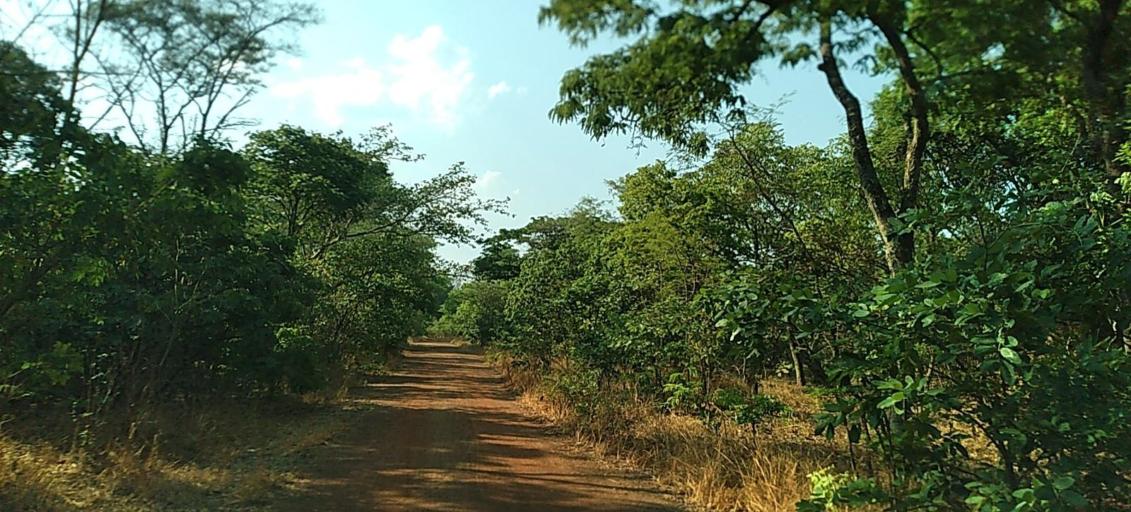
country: ZM
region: Copperbelt
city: Mpongwe
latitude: -13.4482
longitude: 28.0643
